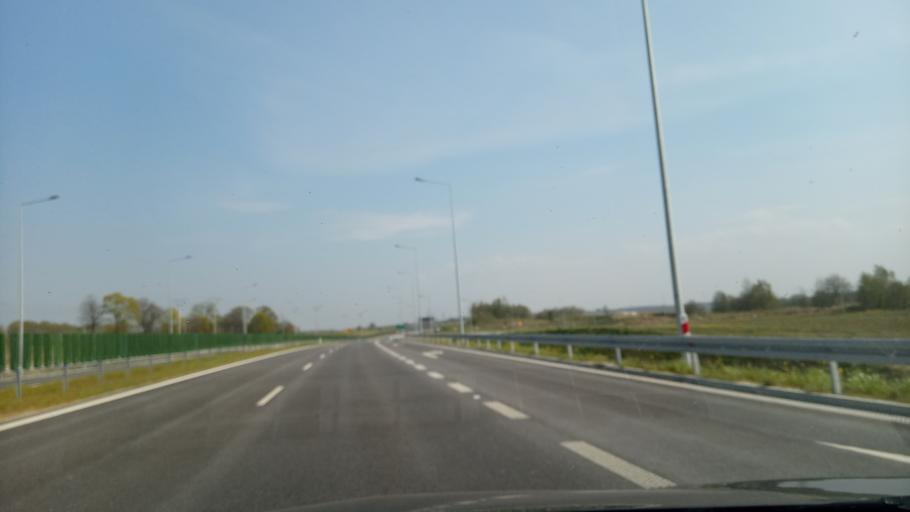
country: PL
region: West Pomeranian Voivodeship
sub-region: Powiat szczecinecki
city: Szczecinek
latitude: 53.7115
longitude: 16.7183
